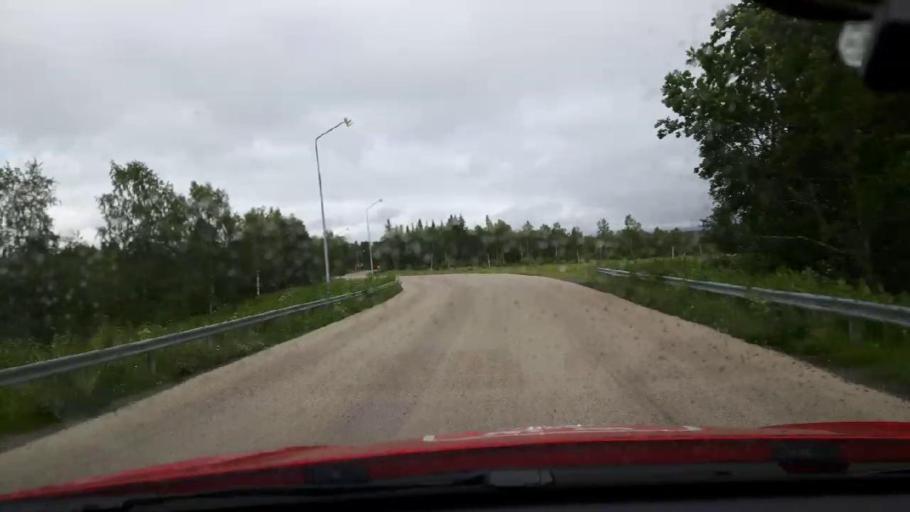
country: SE
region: Jaemtland
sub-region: Are Kommun
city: Are
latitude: 63.2593
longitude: 12.4360
